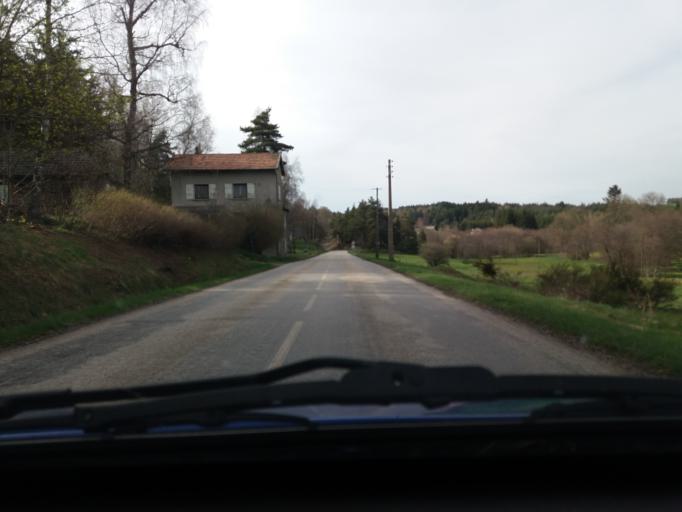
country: FR
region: Auvergne
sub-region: Departement de la Haute-Loire
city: Mazet-Saint-Voy
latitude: 45.0556
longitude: 4.2451
